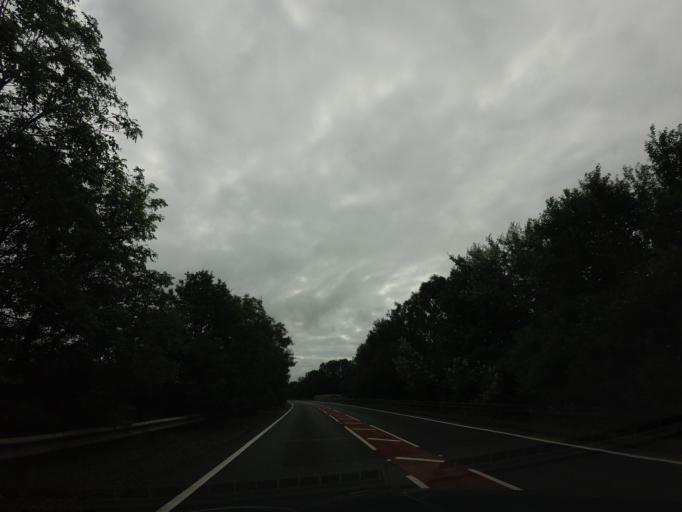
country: GB
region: Scotland
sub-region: Dumfries and Galloway
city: Gretna
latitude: 54.9926
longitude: -3.1160
